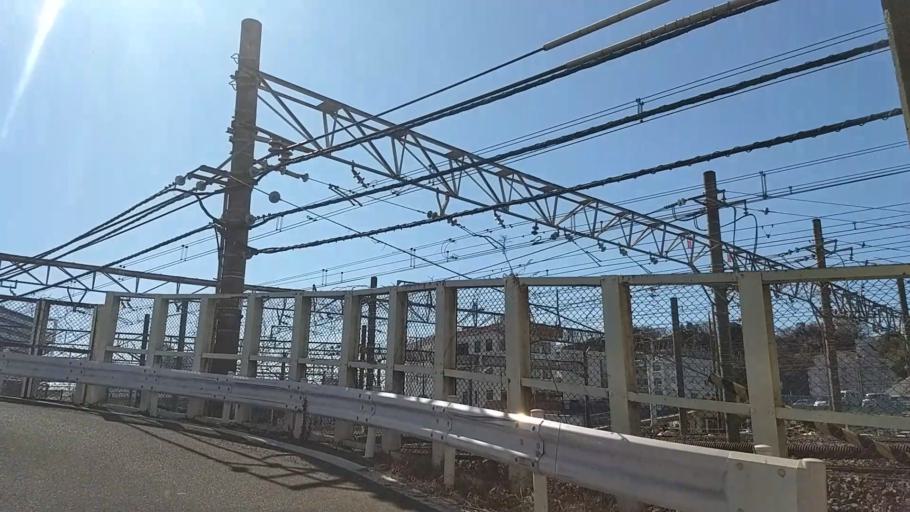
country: JP
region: Kanagawa
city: Kamakura
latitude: 35.3574
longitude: 139.5320
